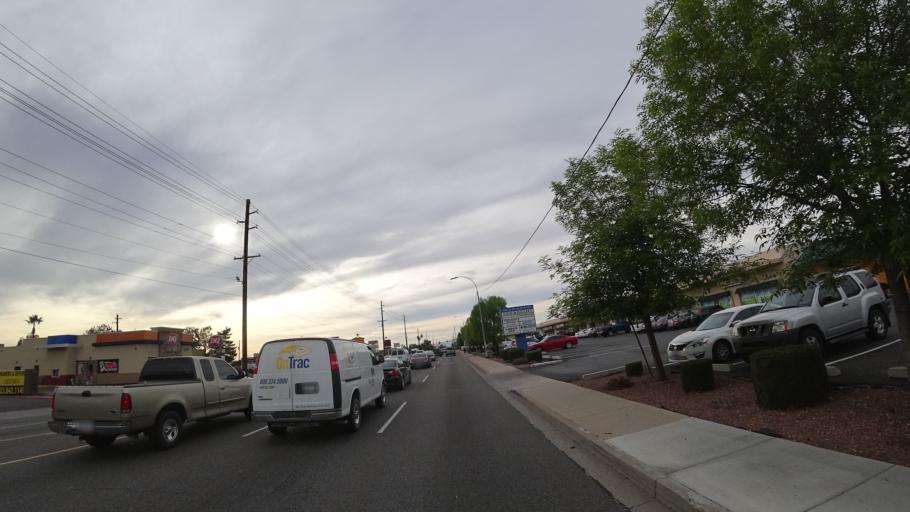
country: US
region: Arizona
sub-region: Maricopa County
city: Glendale
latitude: 33.5676
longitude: -112.1494
